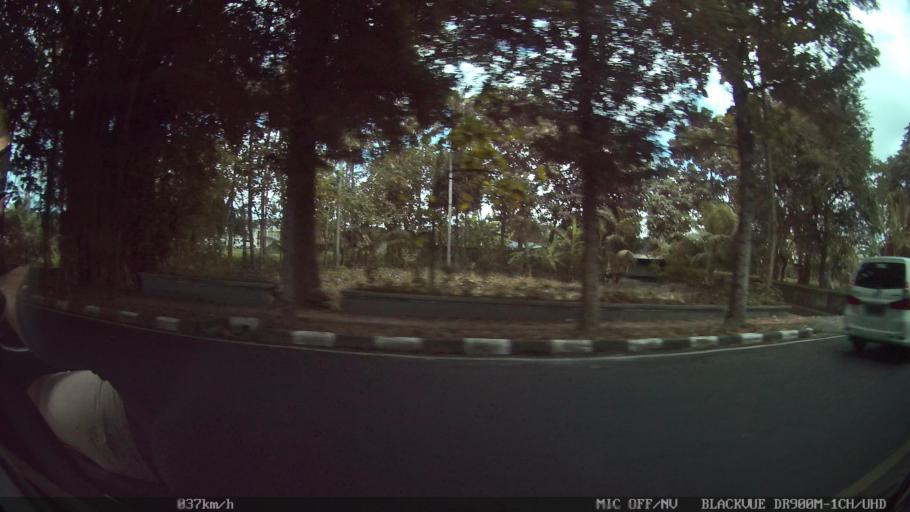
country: ID
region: Bali
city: Banjar Desa
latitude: -8.5815
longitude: 115.2808
